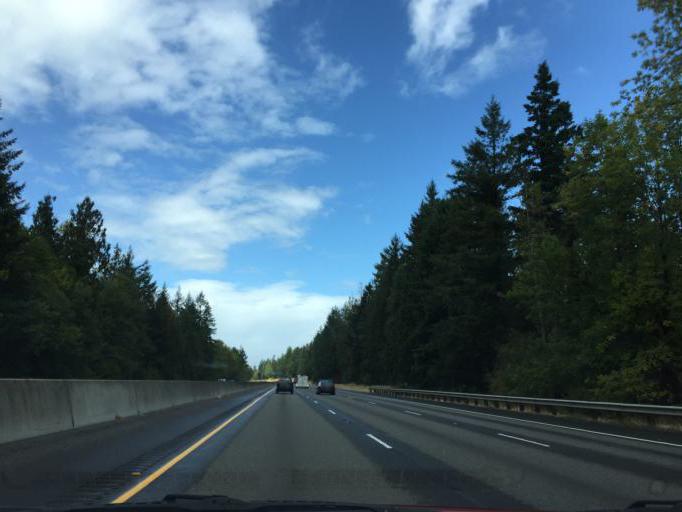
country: US
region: Washington
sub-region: Thurston County
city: Grand Mound
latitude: 46.8551
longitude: -122.9756
